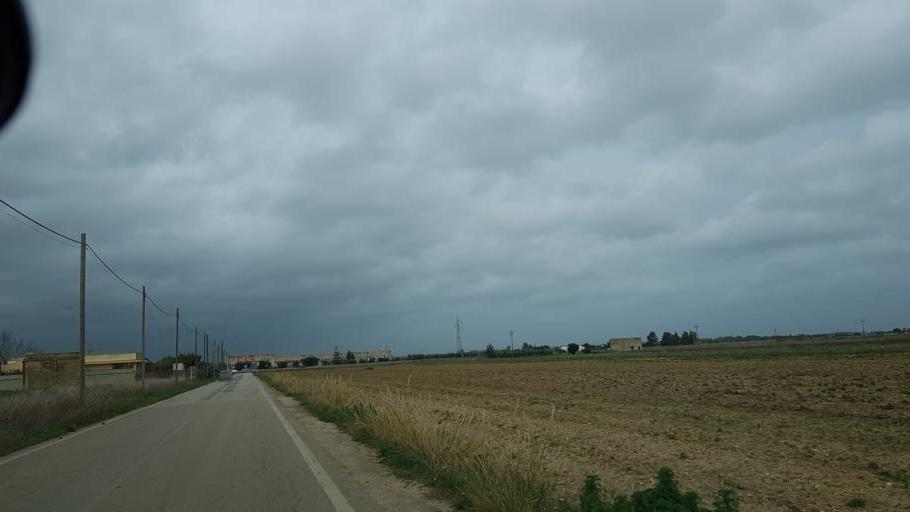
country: IT
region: Apulia
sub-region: Provincia di Brindisi
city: Brindisi
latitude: 40.6053
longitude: 17.8910
